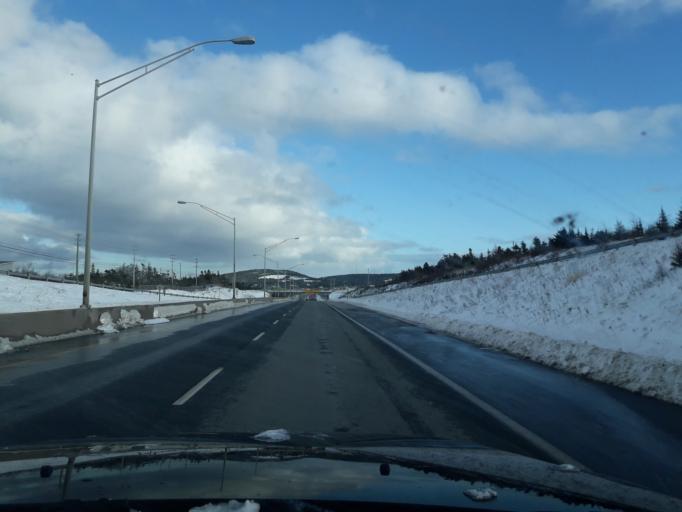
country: CA
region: Newfoundland and Labrador
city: St. John's
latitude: 47.6130
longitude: -52.7112
